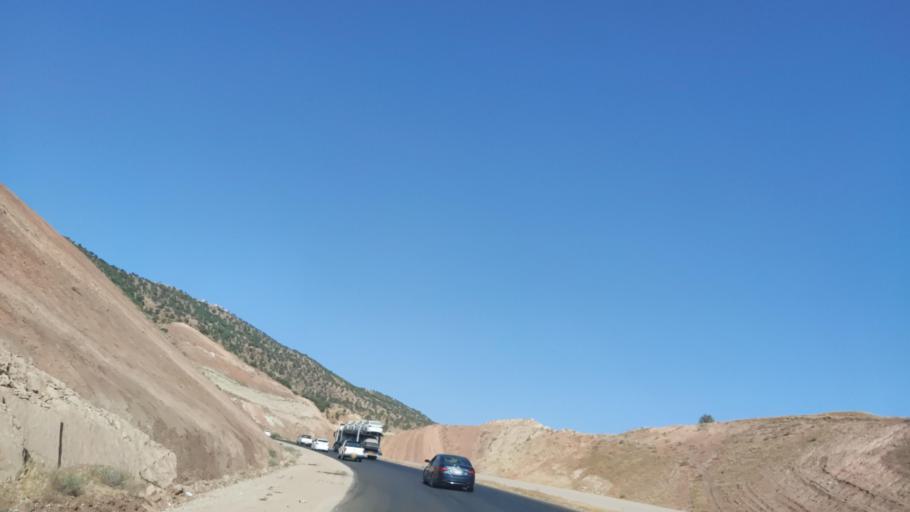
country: IQ
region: Arbil
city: Shaqlawah
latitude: 36.4350
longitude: 44.2994
